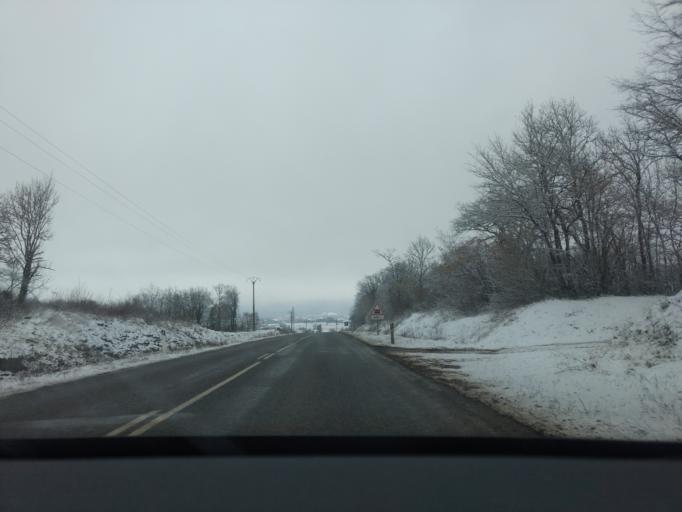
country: FR
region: Franche-Comte
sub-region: Departement du Jura
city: Champagnole
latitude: 46.7805
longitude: 5.8847
